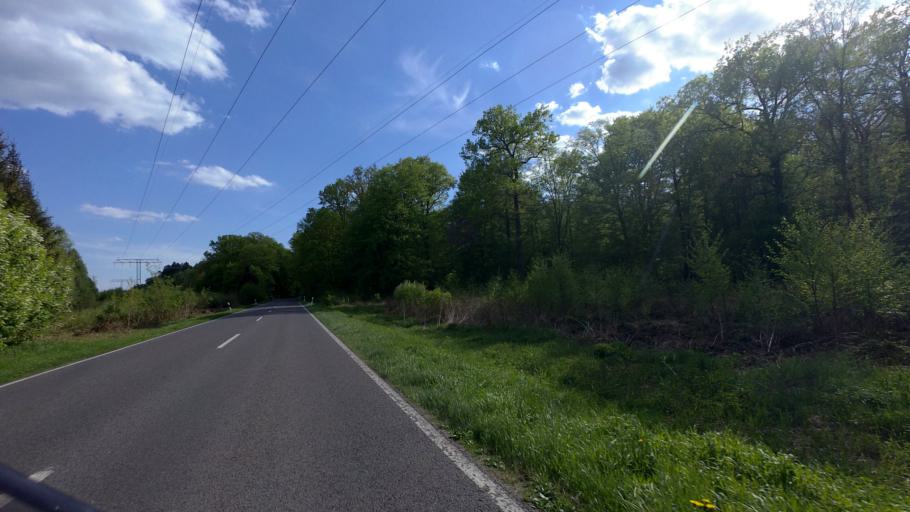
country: DE
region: Brandenburg
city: Liebenwalde
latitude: 52.8201
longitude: 13.4093
